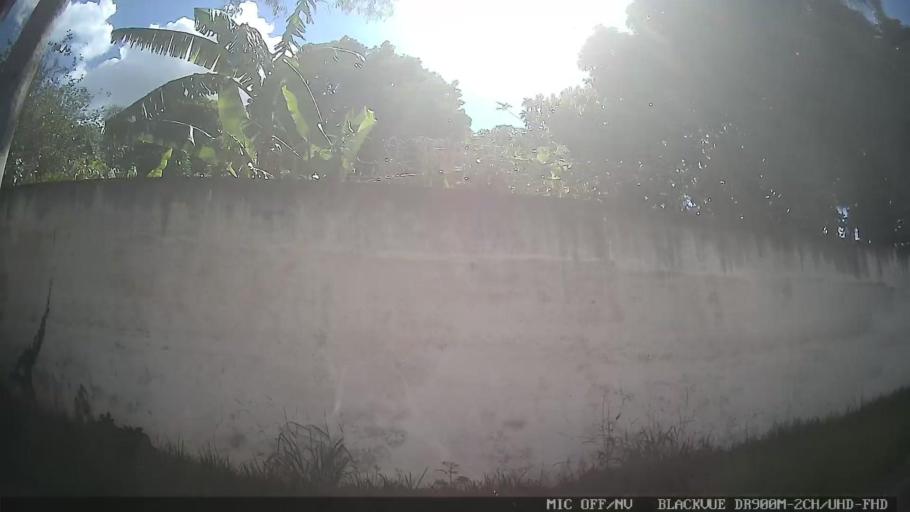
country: BR
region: Sao Paulo
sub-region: Atibaia
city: Atibaia
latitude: -23.1418
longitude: -46.5616
